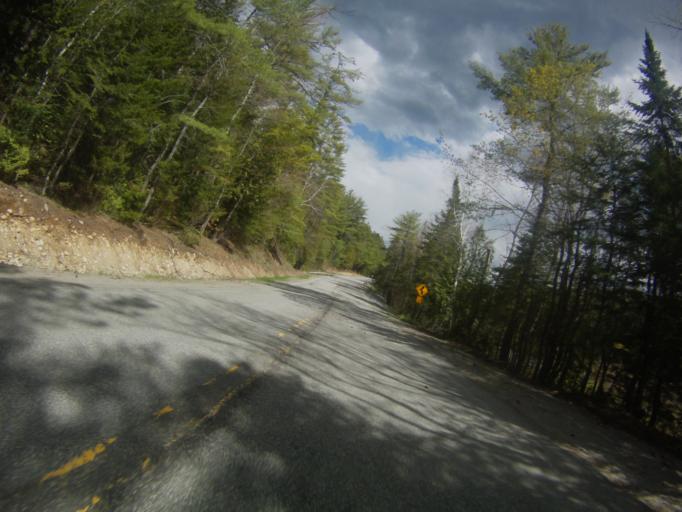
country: US
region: New York
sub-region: Essex County
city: Mineville
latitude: 44.0767
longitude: -73.6543
